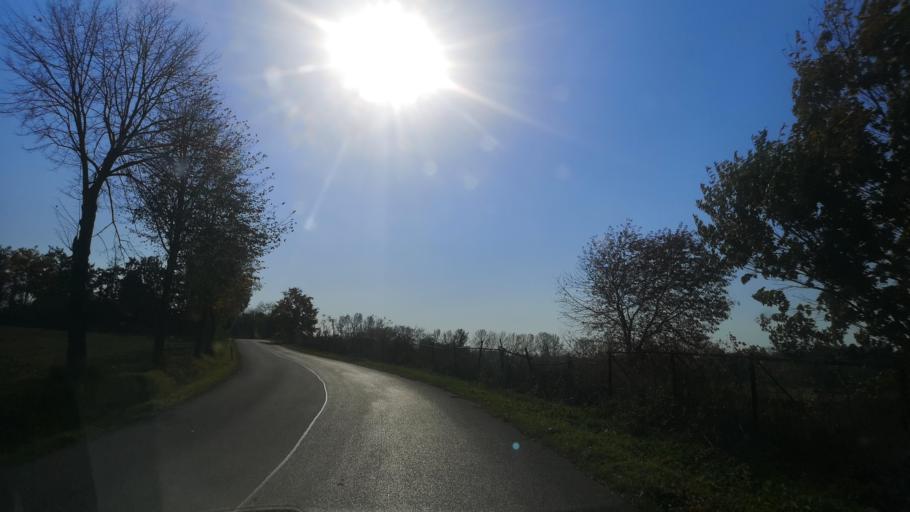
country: SK
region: Nitriansky
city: Zlate Moravce
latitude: 48.4272
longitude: 18.4250
